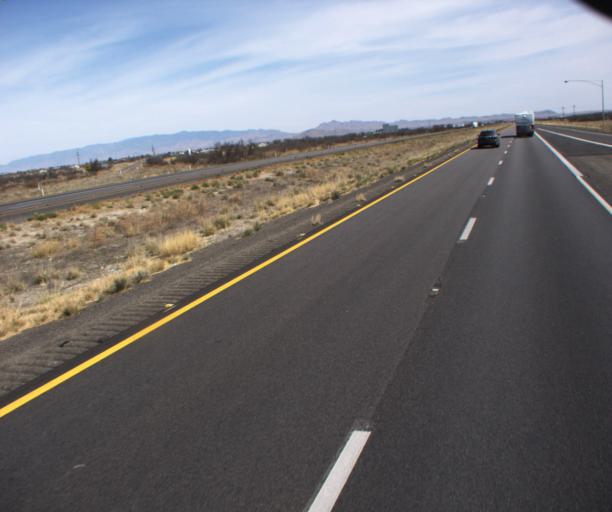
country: US
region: Arizona
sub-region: Cochise County
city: Willcox
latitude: 32.2255
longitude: -109.8755
